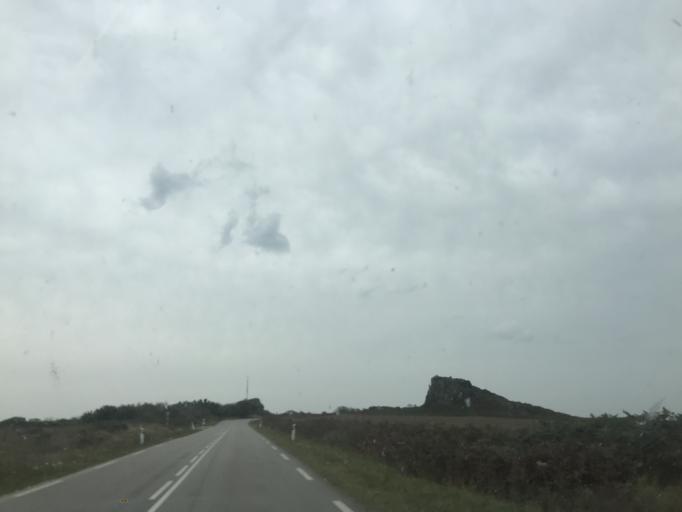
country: FR
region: Brittany
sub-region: Departement du Finistere
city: Plouneour-Menez
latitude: 48.4021
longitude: -3.9190
